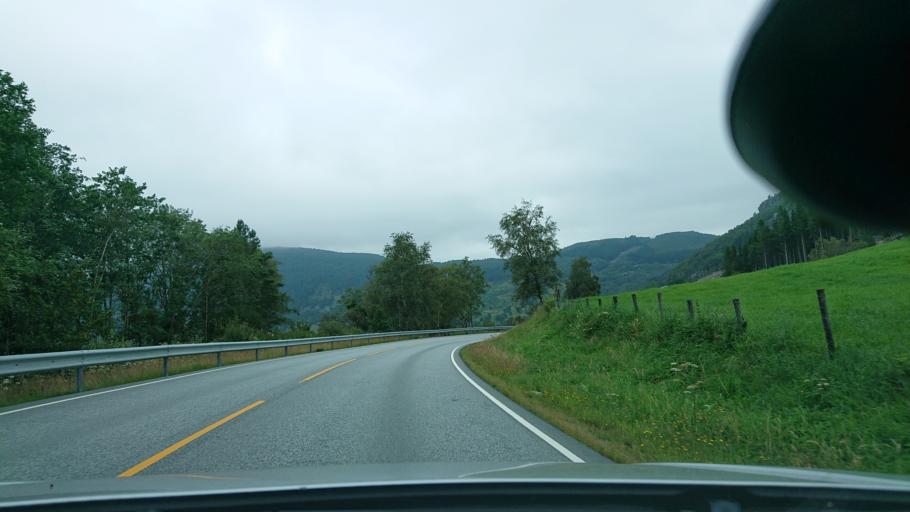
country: NO
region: Rogaland
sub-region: Hjelmeland
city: Hjelmelandsvagen
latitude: 59.1664
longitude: 6.1396
